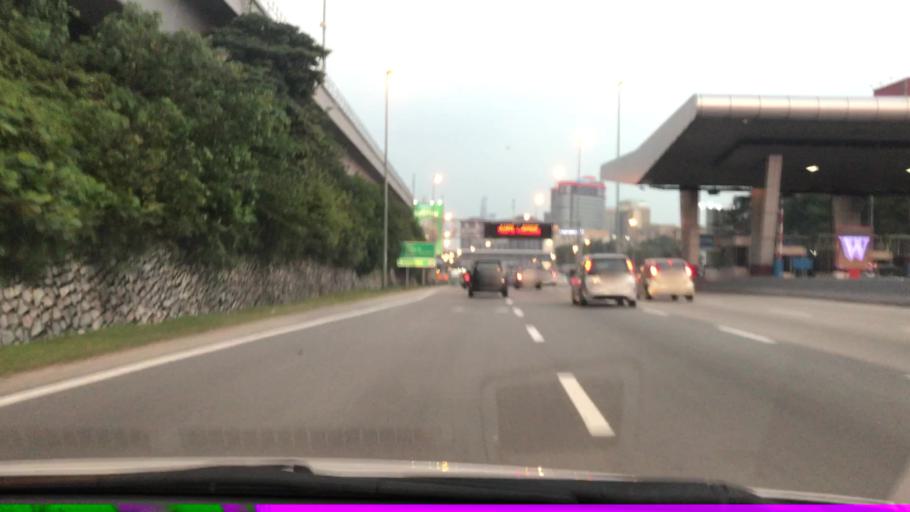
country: MY
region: Selangor
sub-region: Petaling
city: Petaling Jaya
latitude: 3.1311
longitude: 101.6386
